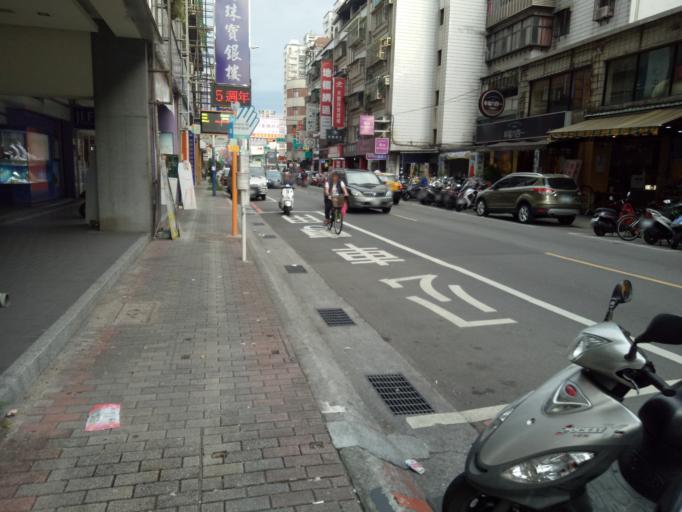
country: TW
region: Taipei
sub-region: Taipei
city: Banqiao
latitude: 25.0492
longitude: 121.4514
